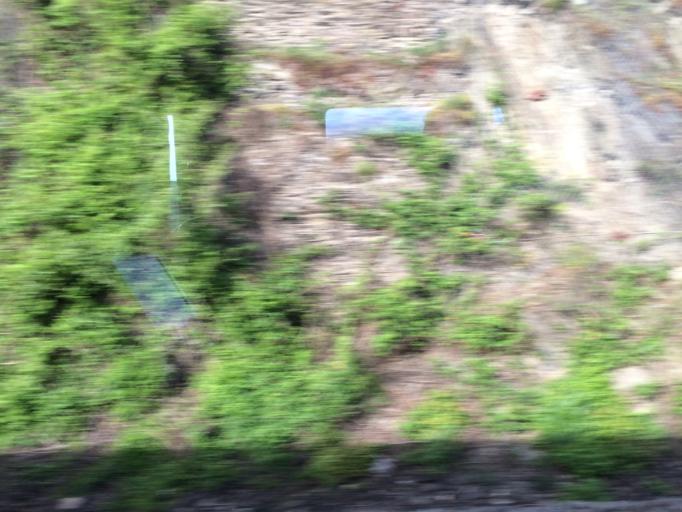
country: DE
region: Rheinland-Pfalz
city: Kestert
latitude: 50.1799
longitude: 7.6476
